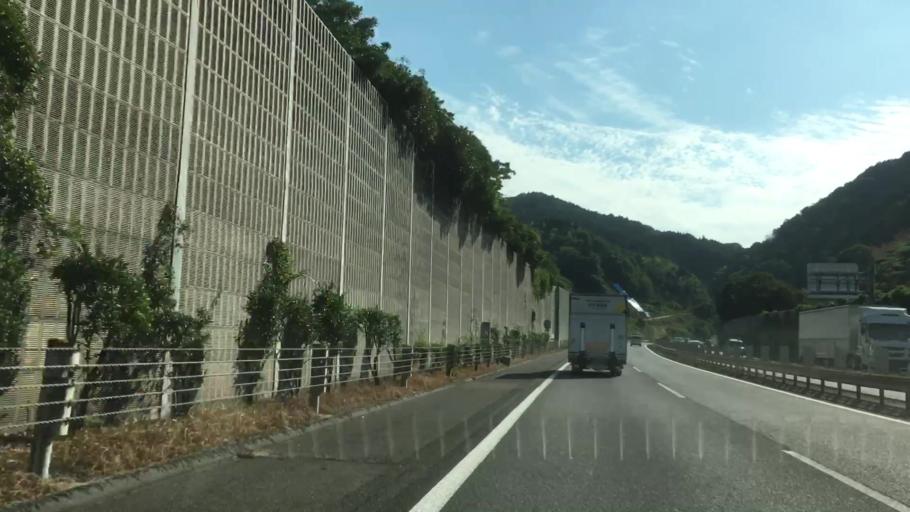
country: JP
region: Yamaguchi
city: Otake
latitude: 34.2345
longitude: 132.2133
